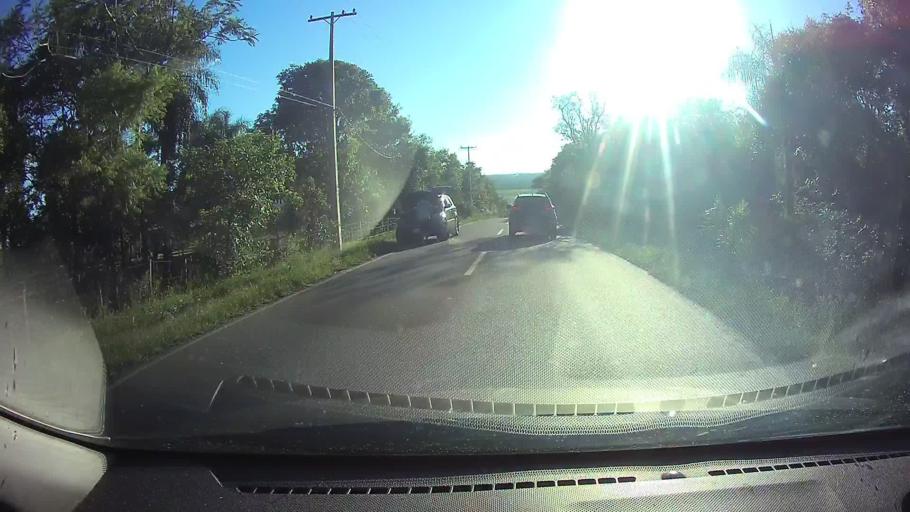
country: PY
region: Cordillera
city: Emboscada
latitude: -25.2052
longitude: -57.3454
